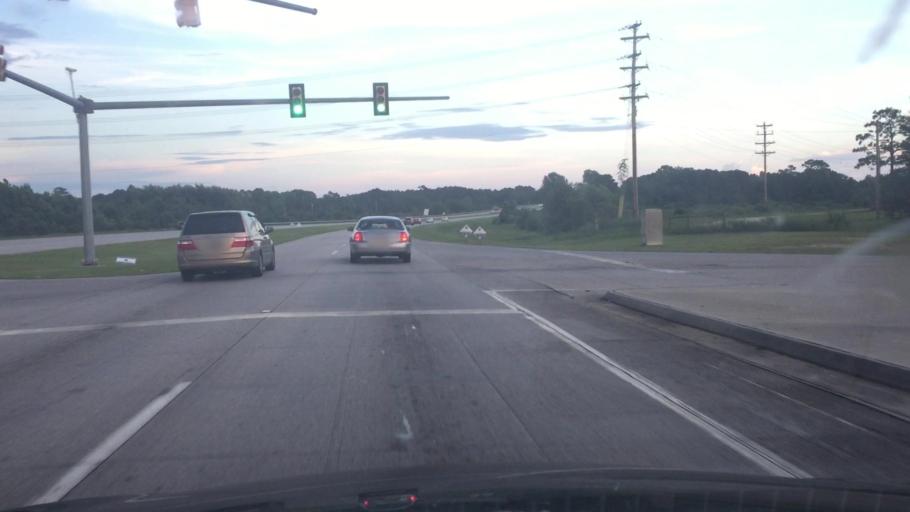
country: US
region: South Carolina
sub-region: Horry County
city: North Myrtle Beach
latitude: 33.8380
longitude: -78.6946
